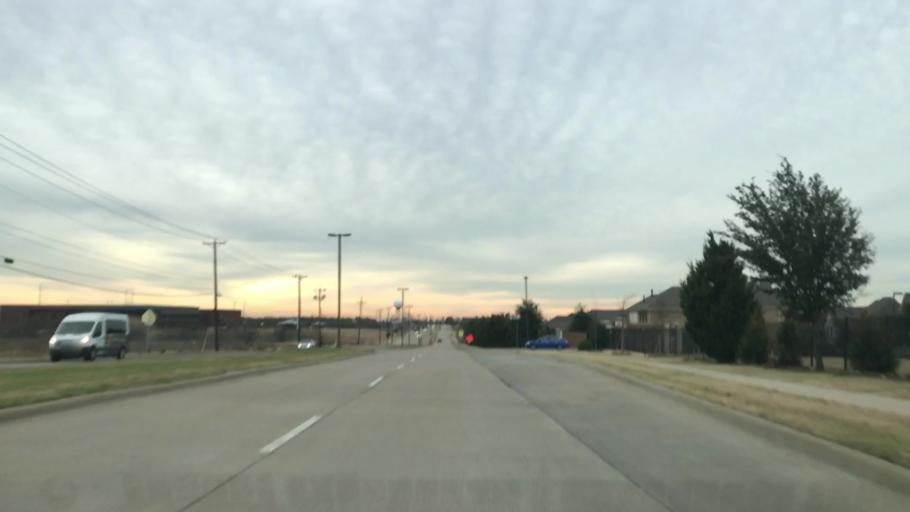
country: US
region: Texas
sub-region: Dallas County
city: Coppell
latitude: 32.9255
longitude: -96.9794
